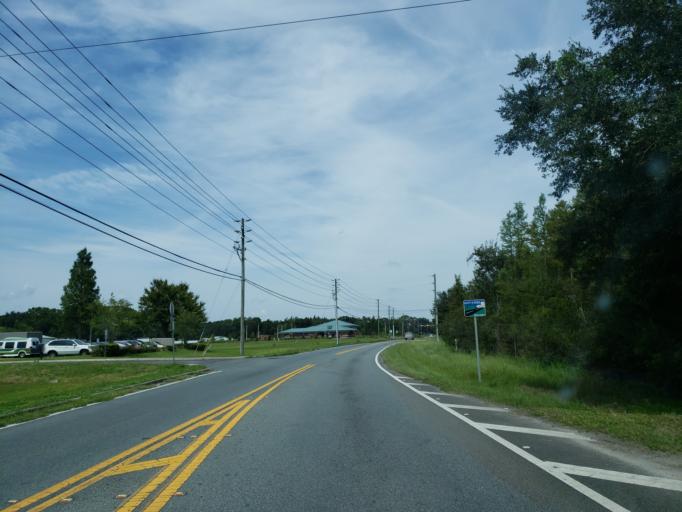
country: US
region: Florida
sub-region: Pasco County
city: Wesley Chapel
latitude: 28.2409
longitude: -82.3648
